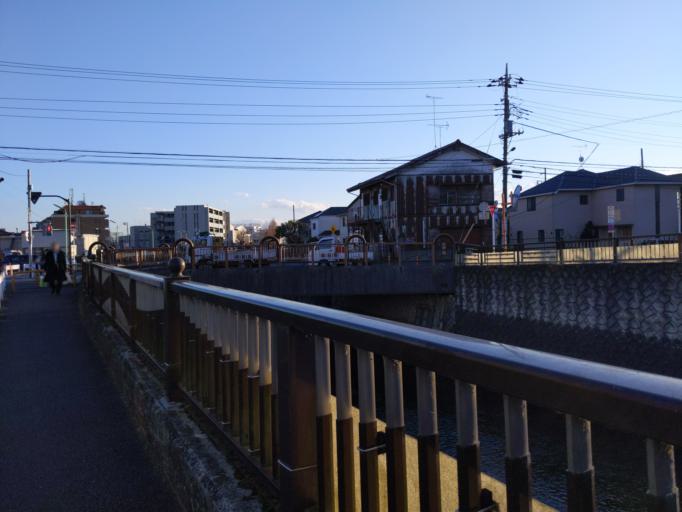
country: JP
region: Tokyo
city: Chofugaoka
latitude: 35.6245
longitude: 139.6130
